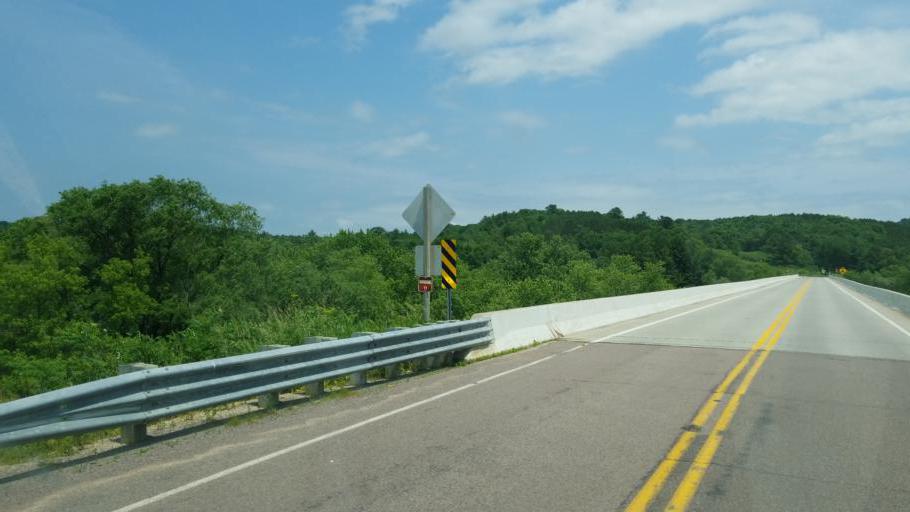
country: US
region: Wisconsin
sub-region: Monroe County
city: Cashton
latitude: 43.6397
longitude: -90.6005
